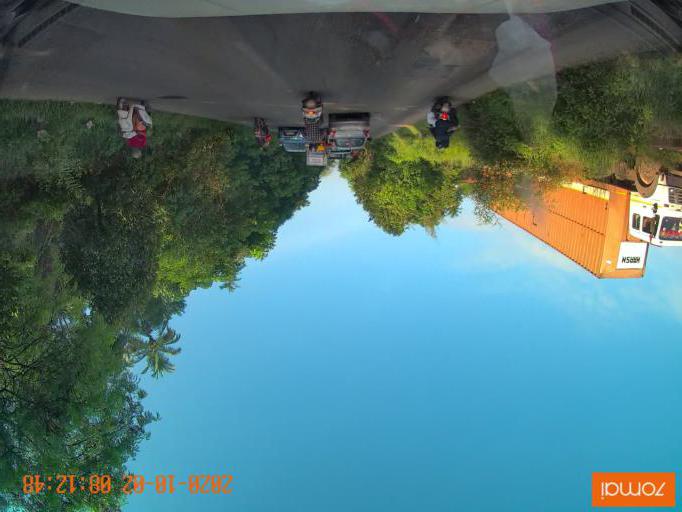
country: IN
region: Kerala
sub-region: Kozhikode
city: Kozhikode
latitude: 11.2839
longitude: 75.8024
